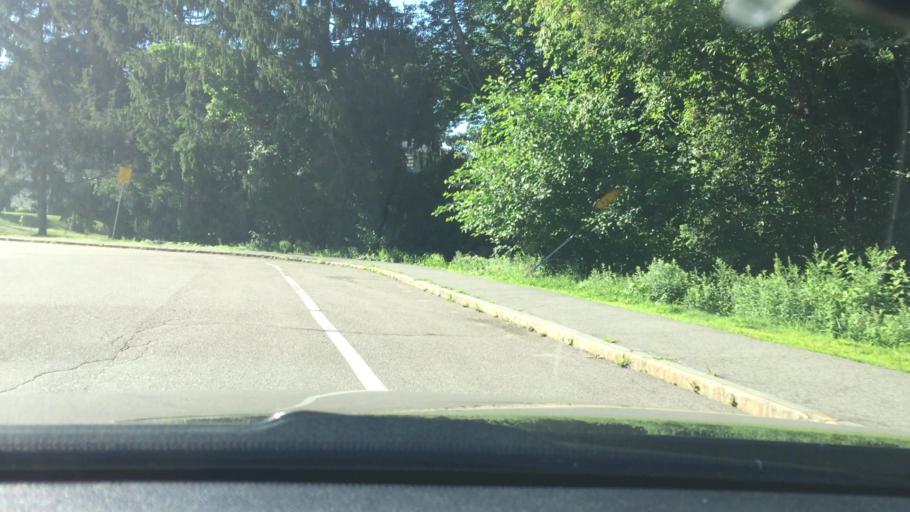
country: US
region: Massachusetts
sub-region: Norfolk County
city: Needham
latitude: 42.2945
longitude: -71.2404
